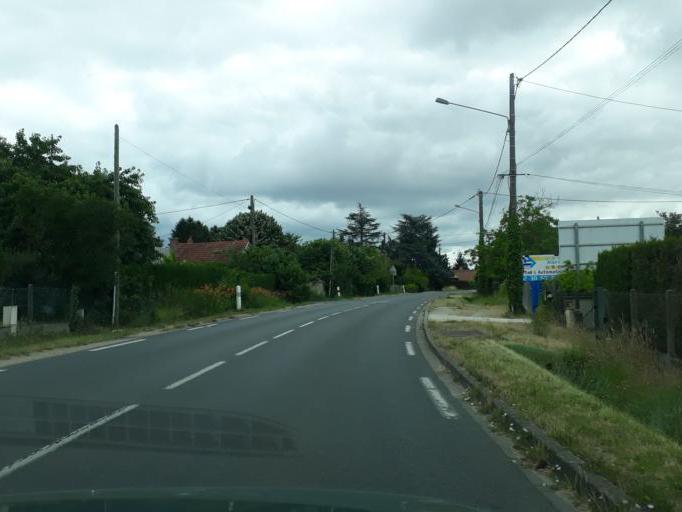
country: FR
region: Centre
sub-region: Departement du Loiret
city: Sandillon
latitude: 47.8517
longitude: 2.0165
